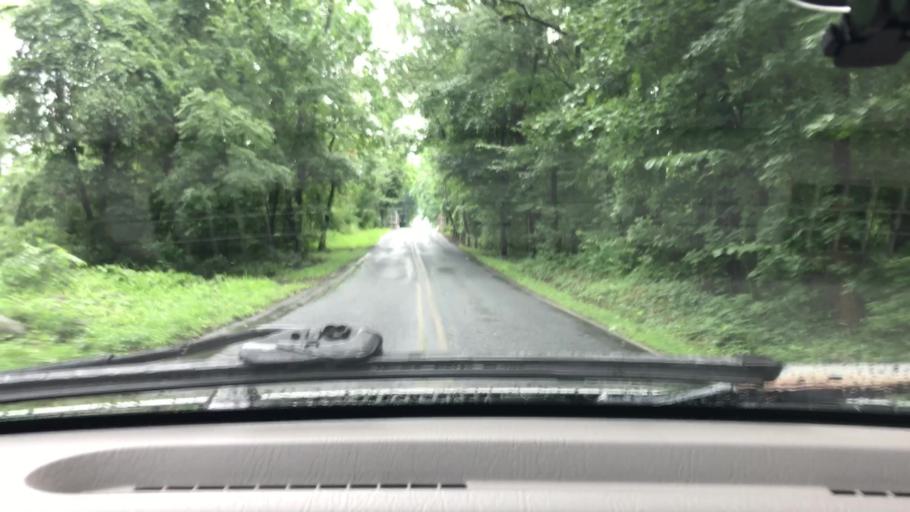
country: US
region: Pennsylvania
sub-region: Lancaster County
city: Elizabethtown
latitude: 40.2104
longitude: -76.6205
